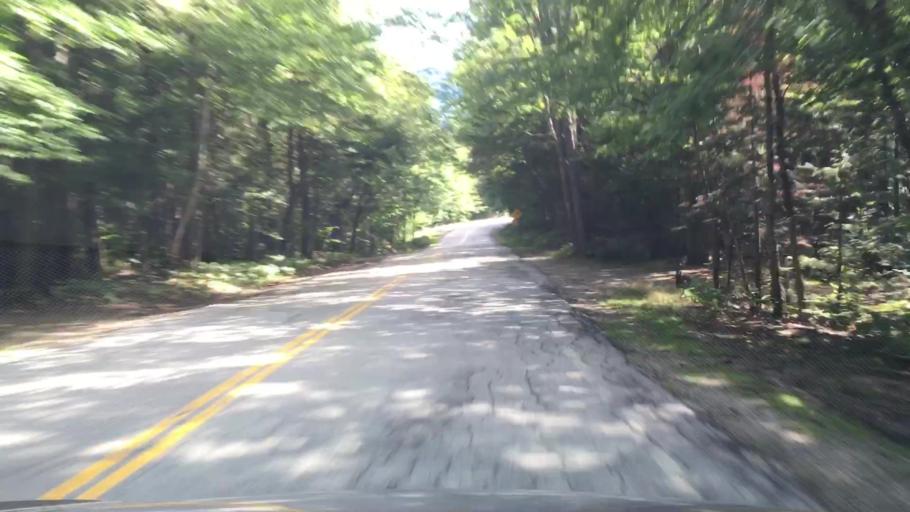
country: US
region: New Hampshire
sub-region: Carroll County
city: Tamworth
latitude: 43.9995
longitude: -71.3223
